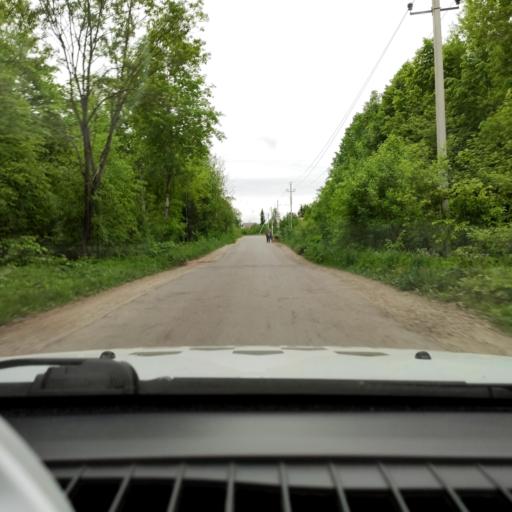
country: RU
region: Perm
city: Novyye Lyady
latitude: 58.0424
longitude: 56.6205
